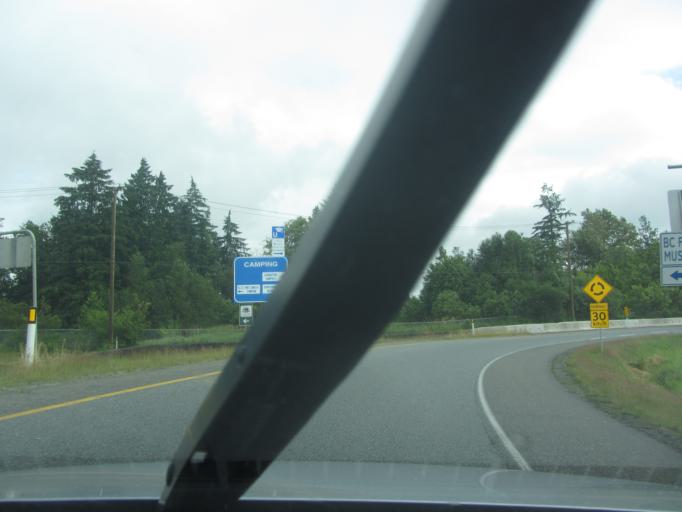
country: CA
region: British Columbia
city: Langley
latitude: 49.1379
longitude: -122.5831
